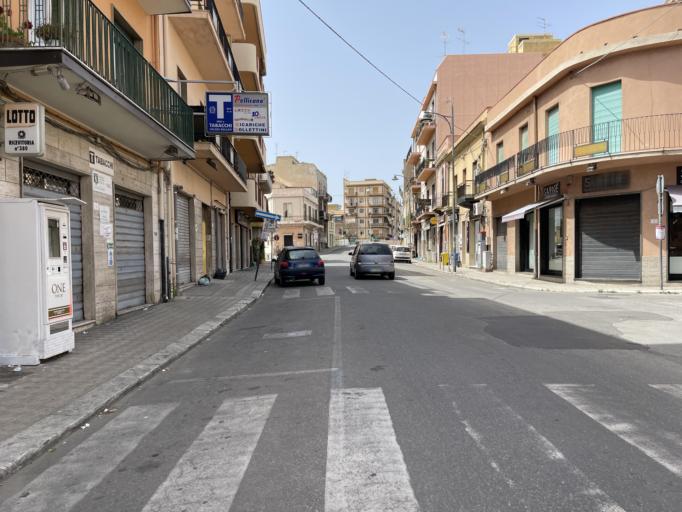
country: IT
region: Calabria
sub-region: Provincia di Reggio Calabria
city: Reggio Calabria
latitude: 38.1004
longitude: 15.6424
